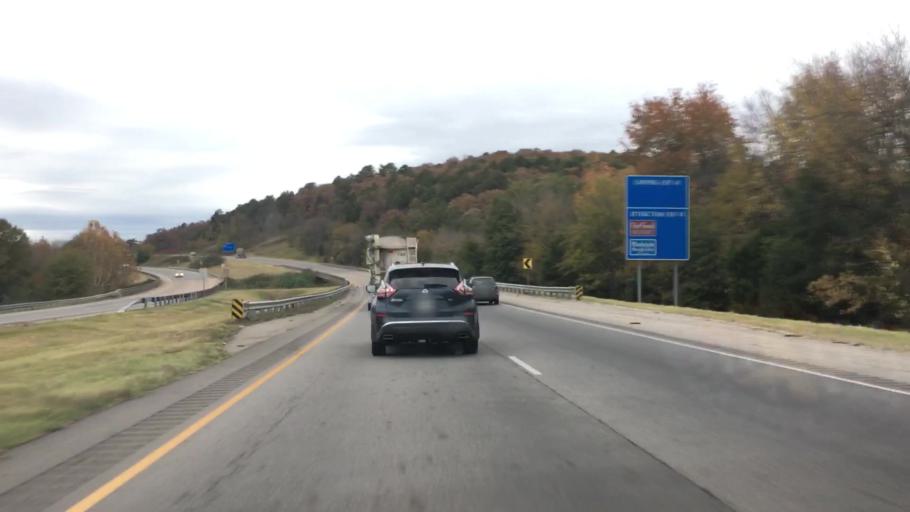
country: US
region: Arkansas
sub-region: Johnson County
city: Coal Hill
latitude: 35.5025
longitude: -93.7282
